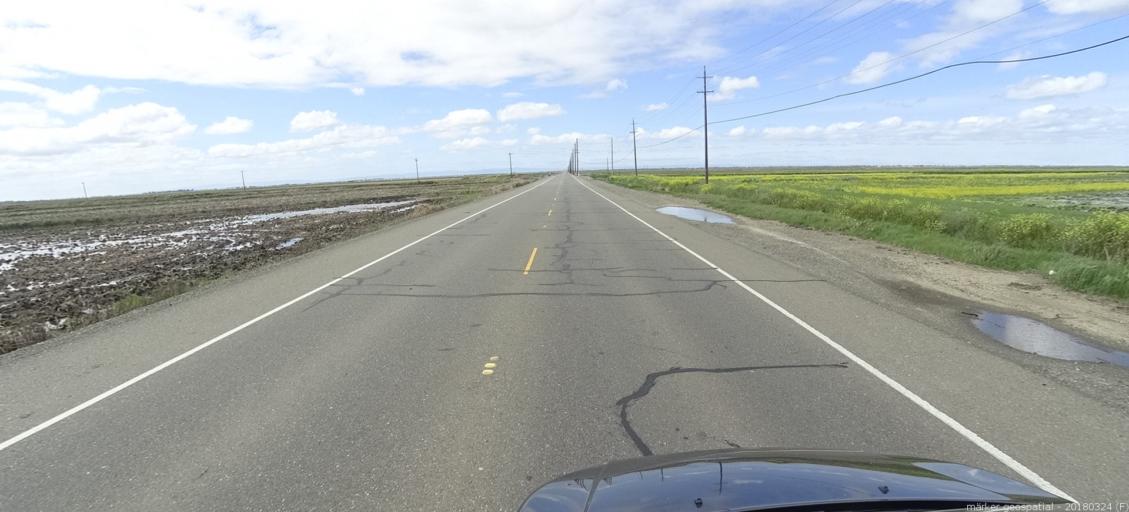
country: US
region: California
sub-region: Sacramento County
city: Elverta
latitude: 38.7144
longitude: -121.5091
